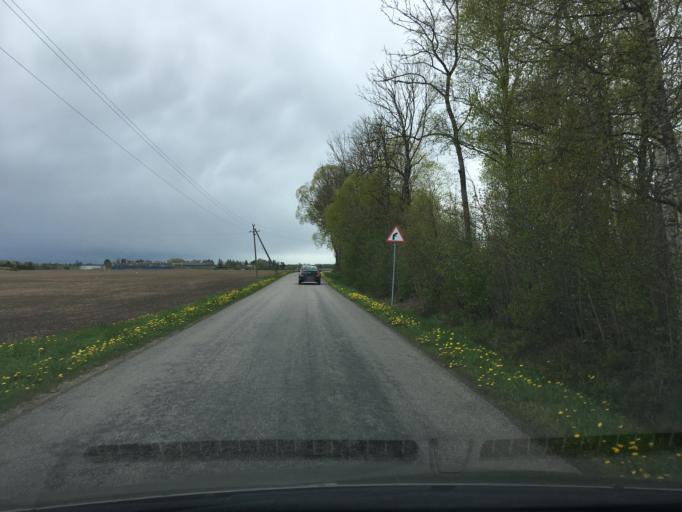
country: EE
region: Harju
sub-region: Joelaehtme vald
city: Loo
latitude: 59.3735
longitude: 24.9658
